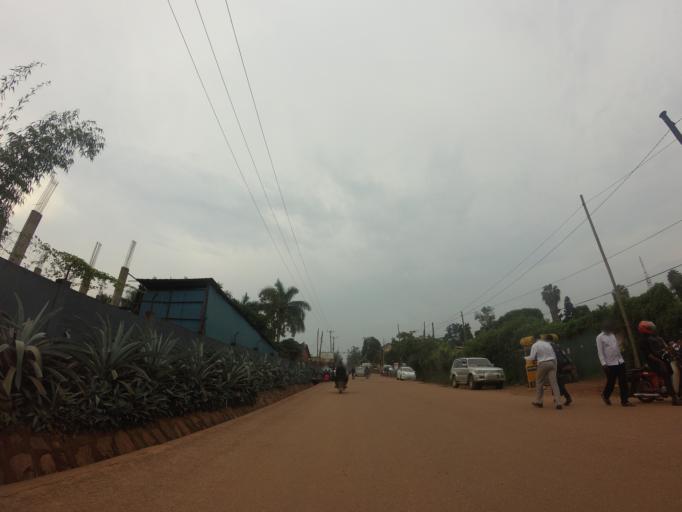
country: UG
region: Central Region
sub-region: Wakiso District
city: Kireka
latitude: 0.3400
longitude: 32.6256
